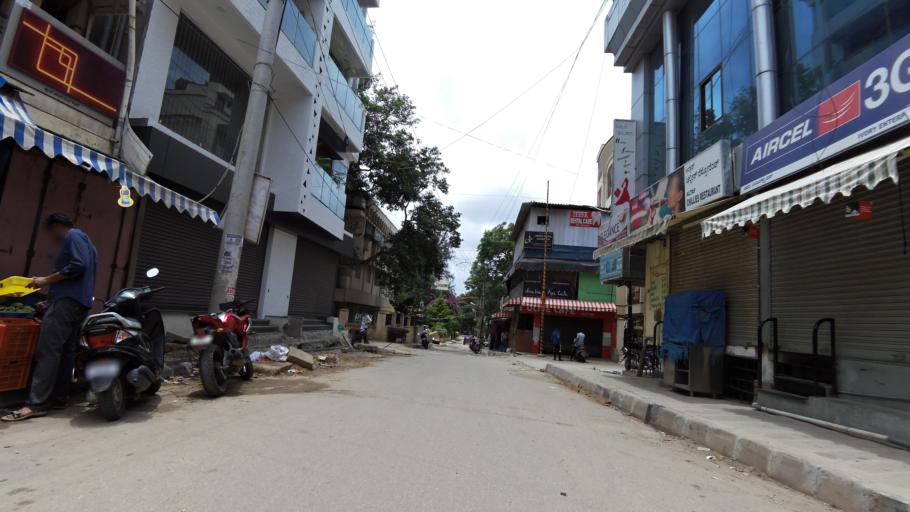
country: IN
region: Karnataka
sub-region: Bangalore Urban
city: Bangalore
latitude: 13.0039
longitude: 77.6228
